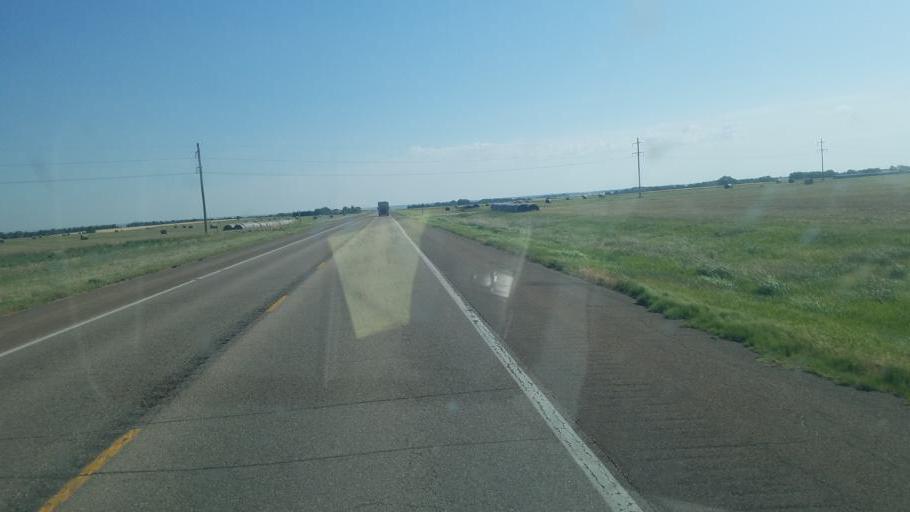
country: US
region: Kansas
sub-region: Barton County
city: Great Bend
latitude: 38.3898
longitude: -98.6774
